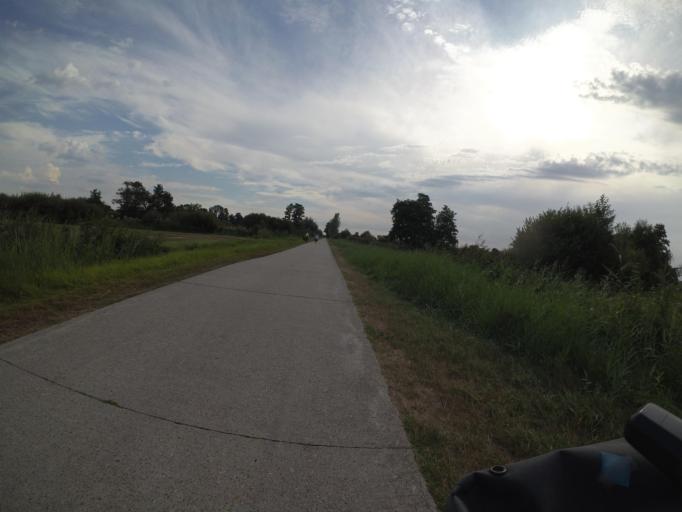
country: NL
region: Overijssel
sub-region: Gemeente Zwartewaterland
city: Hasselt
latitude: 52.6424
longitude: 6.1152
